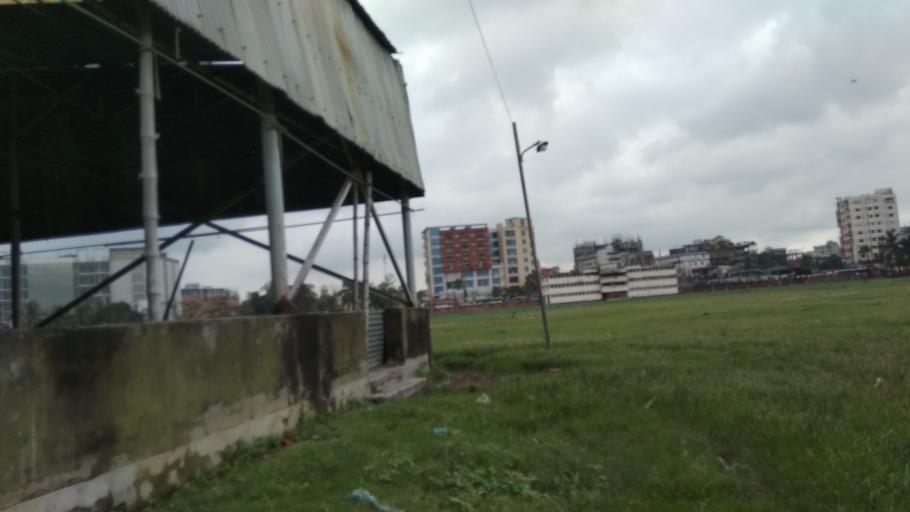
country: BD
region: Dhaka
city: Tungi
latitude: 23.8927
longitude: 90.3994
